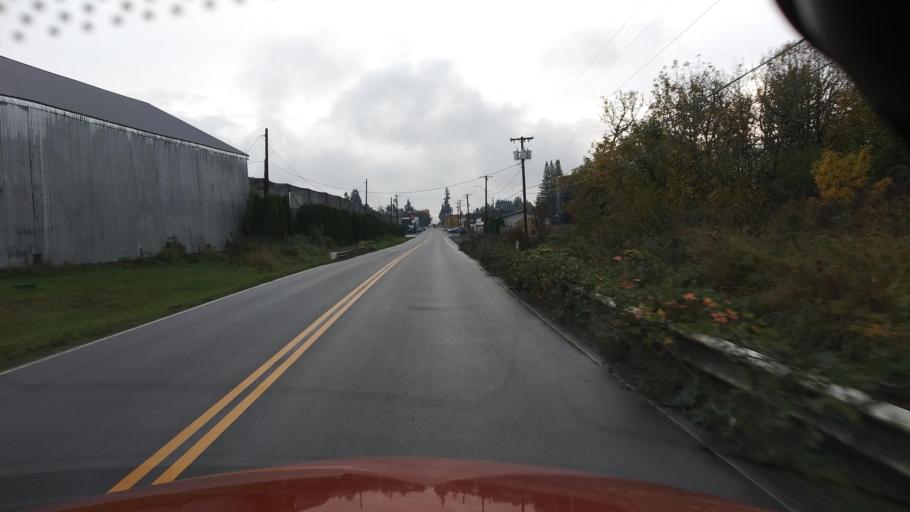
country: US
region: Oregon
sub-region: Washington County
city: North Plains
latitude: 45.5986
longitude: -123.0095
